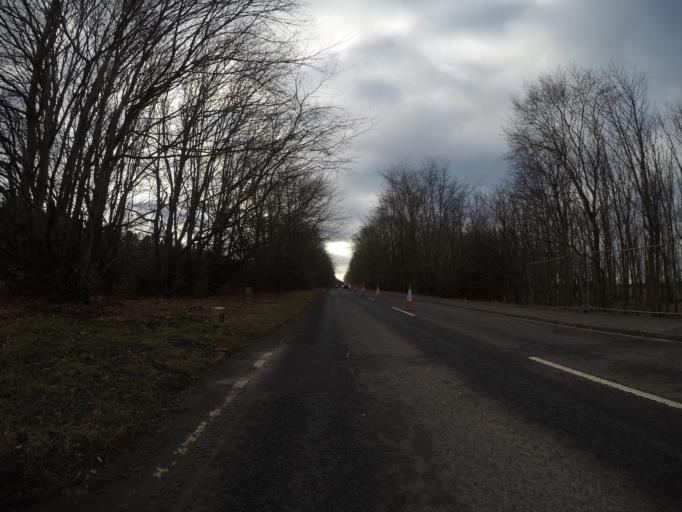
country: GB
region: Scotland
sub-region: North Ayrshire
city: Dreghorn
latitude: 55.5849
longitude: -4.6467
